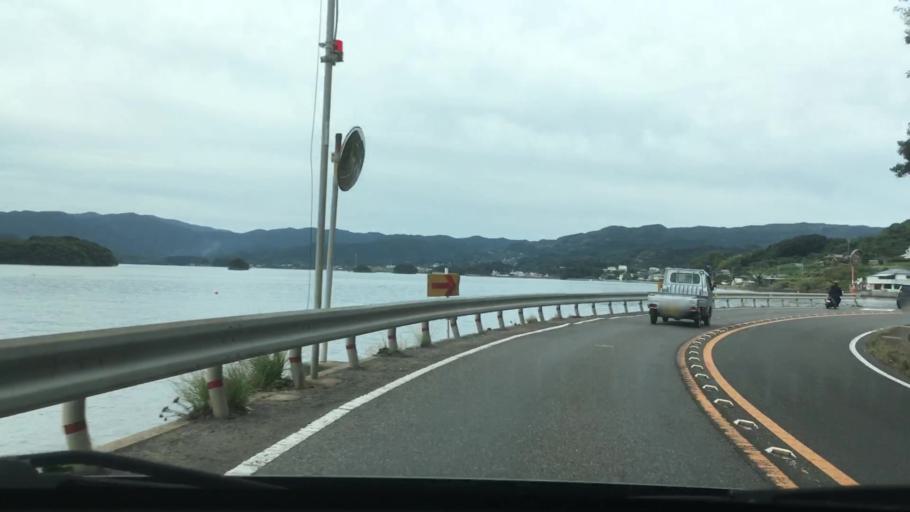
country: JP
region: Nagasaki
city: Sasebo
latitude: 33.0291
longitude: 129.7433
